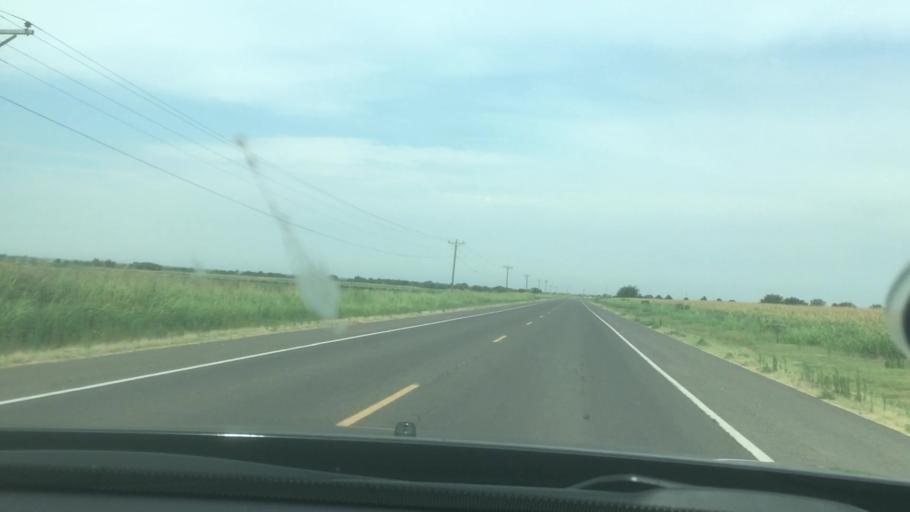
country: US
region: Oklahoma
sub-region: Garvin County
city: Maysville
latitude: 34.8192
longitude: -97.4783
